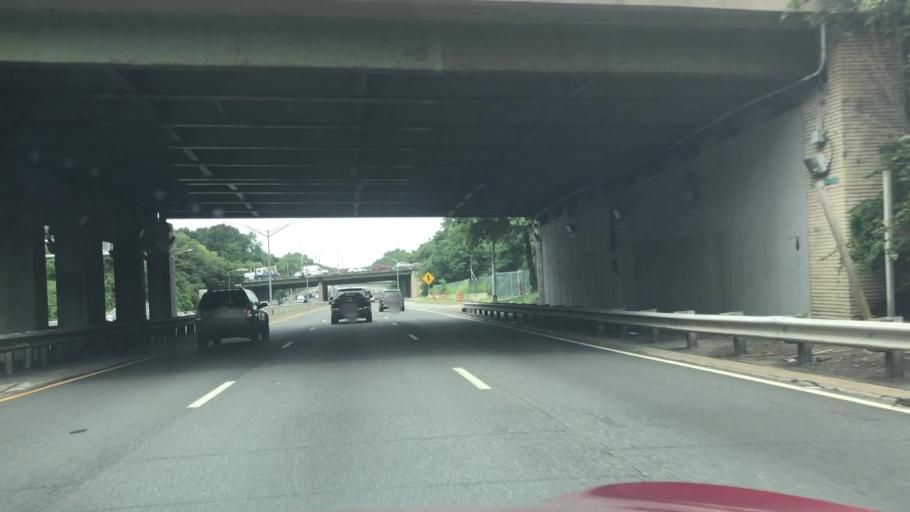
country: US
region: New York
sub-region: Nassau County
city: Bellerose Terrace
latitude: 40.7422
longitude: -73.7705
